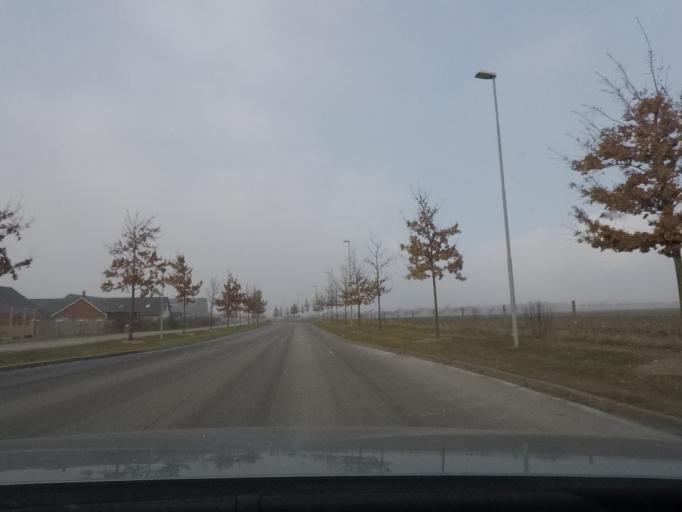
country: SE
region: Skane
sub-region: Malmo
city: Bunkeflostrand
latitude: 55.5461
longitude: 12.9291
